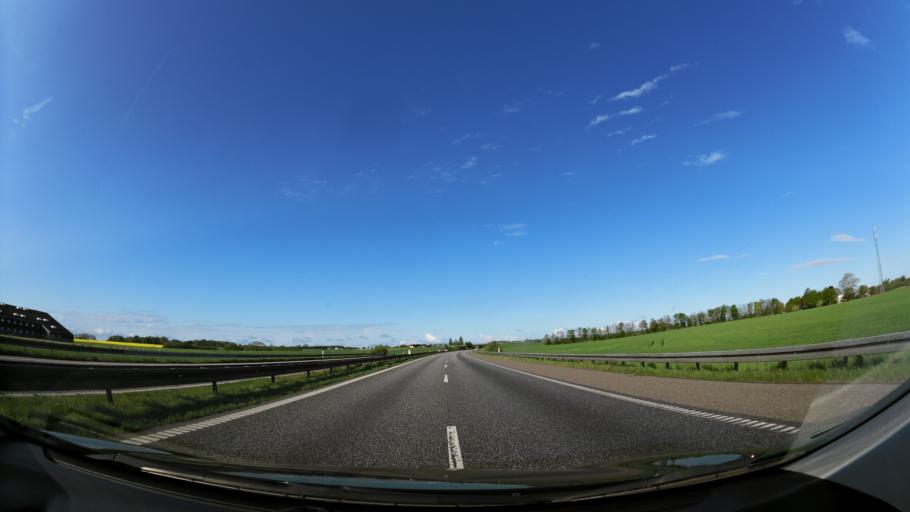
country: DK
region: Central Jutland
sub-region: Hedensted Kommune
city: Hedensted
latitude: 55.7729
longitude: 9.6487
